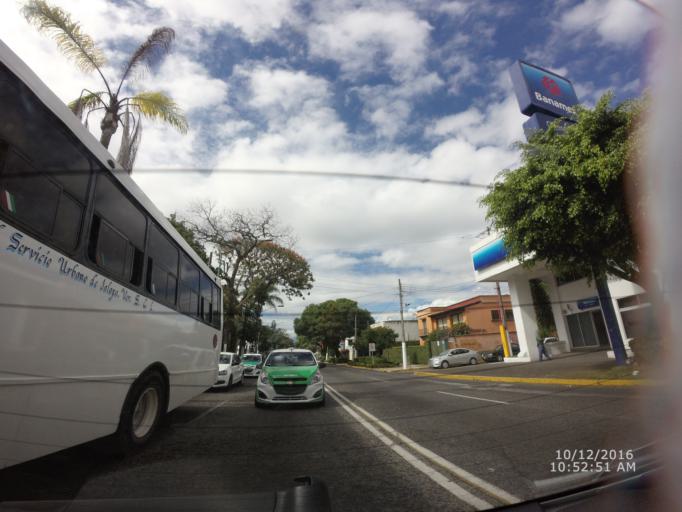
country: MX
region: Veracruz
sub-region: Xalapa
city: Xalapa de Enriquez
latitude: 19.5389
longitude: -96.9280
